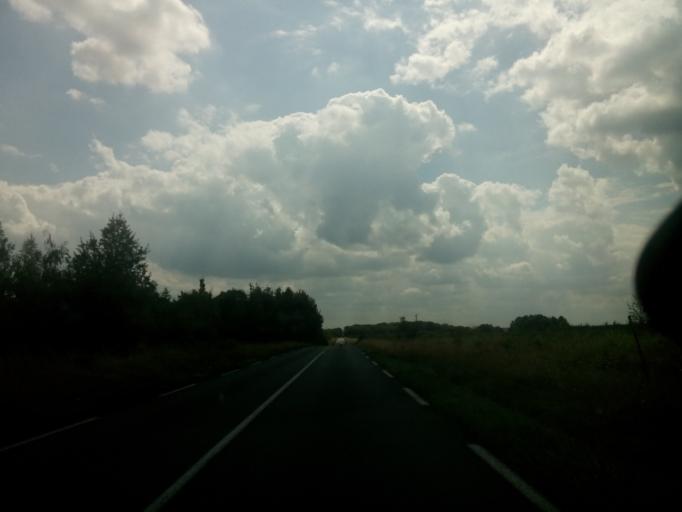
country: FR
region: Centre
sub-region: Departement d'Indre-et-Loire
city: Cheille
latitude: 47.2887
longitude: 0.4218
